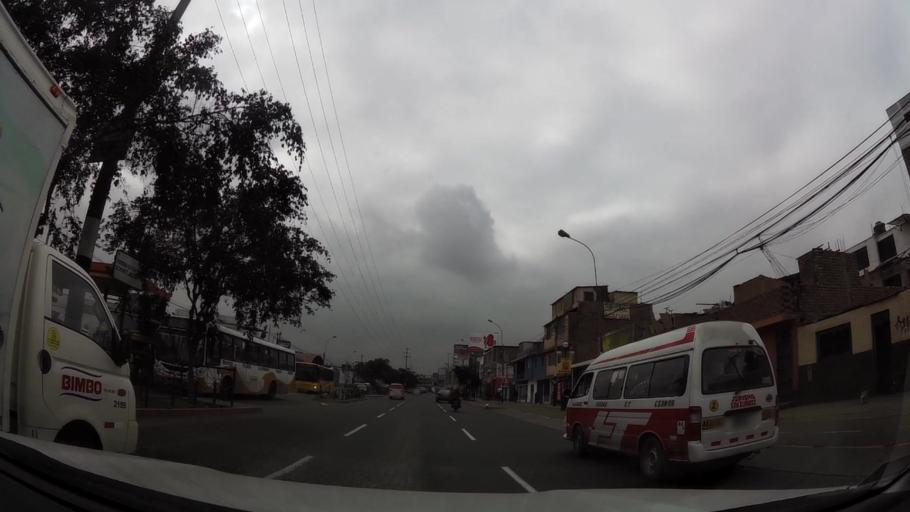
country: PE
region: Lima
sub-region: Lima
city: Surco
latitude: -12.1842
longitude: -77.0035
